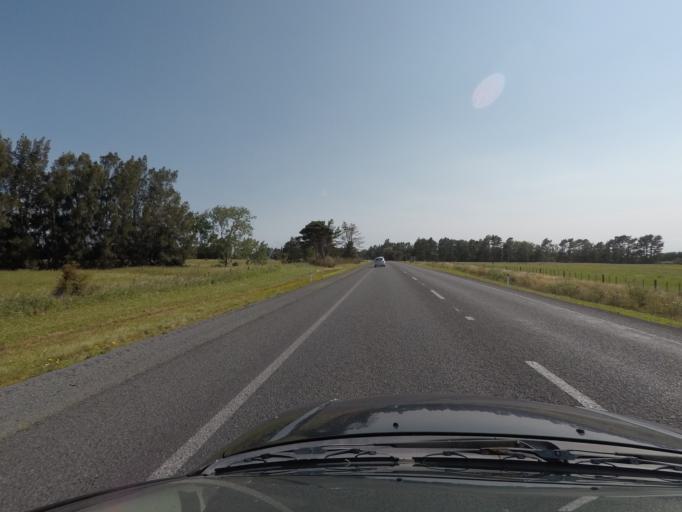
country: NZ
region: Northland
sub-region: Whangarei
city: Ruakaka
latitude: -35.9621
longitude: 174.4476
